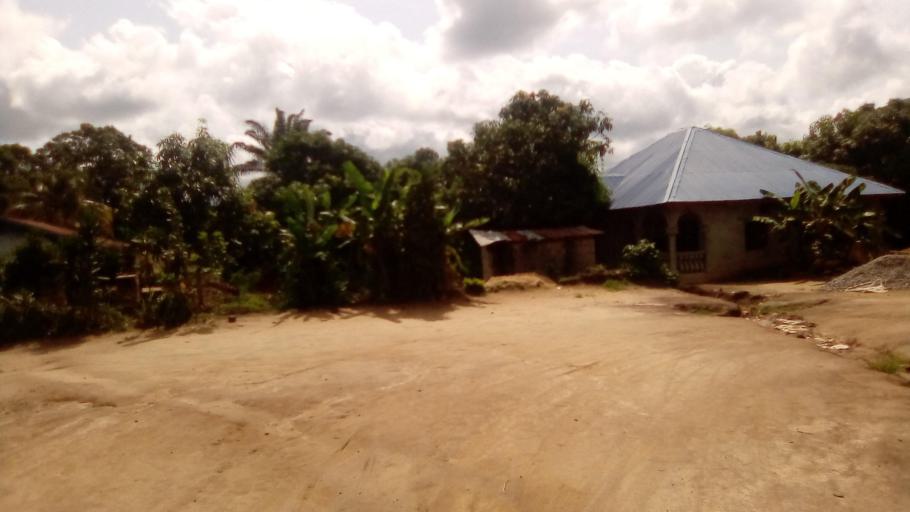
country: SL
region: Southern Province
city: Baoma
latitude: 7.9808
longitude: -11.7249
